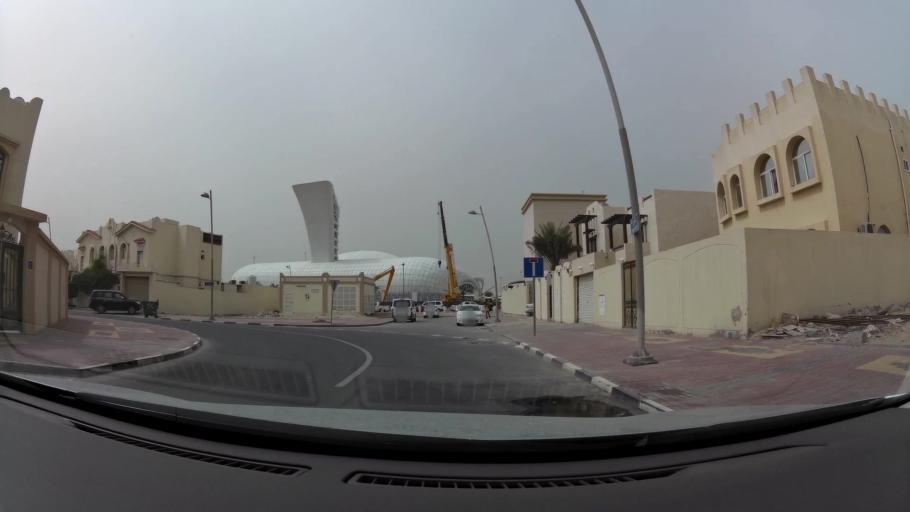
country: QA
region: Baladiyat ad Dawhah
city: Doha
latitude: 25.2361
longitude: 51.5488
